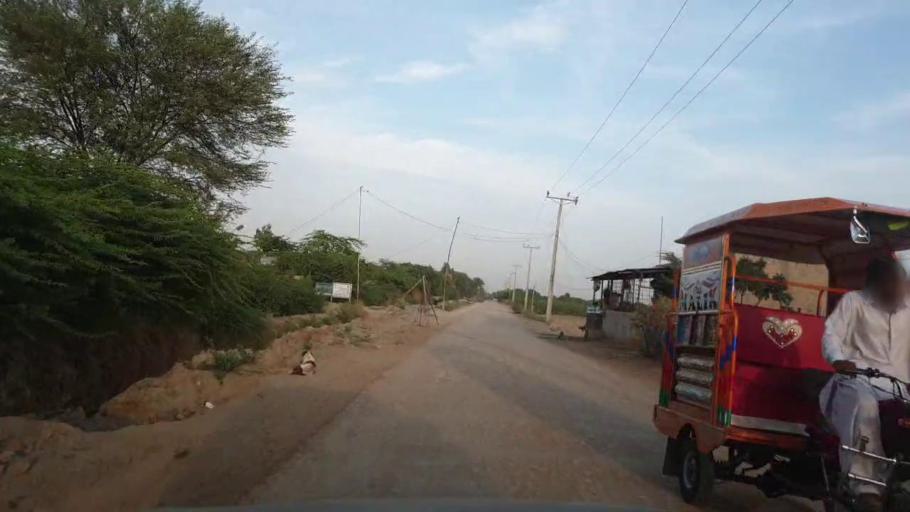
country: PK
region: Sindh
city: Kunri
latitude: 25.1607
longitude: 69.5572
